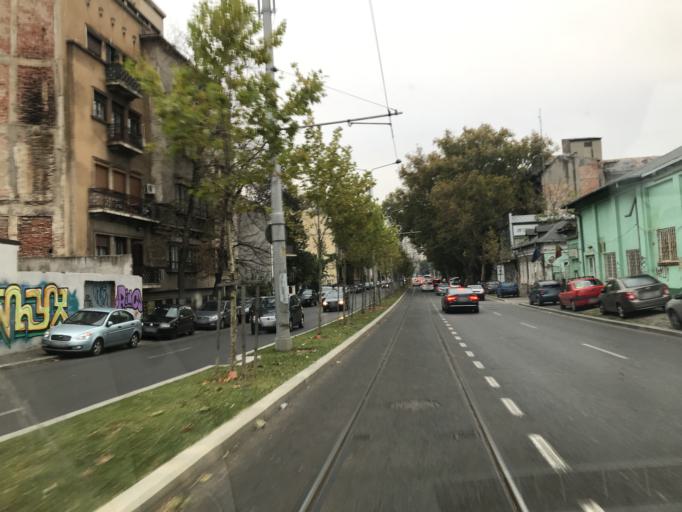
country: RO
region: Bucuresti
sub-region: Municipiul Bucuresti
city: Bucuresti
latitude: 44.4391
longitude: 26.0821
